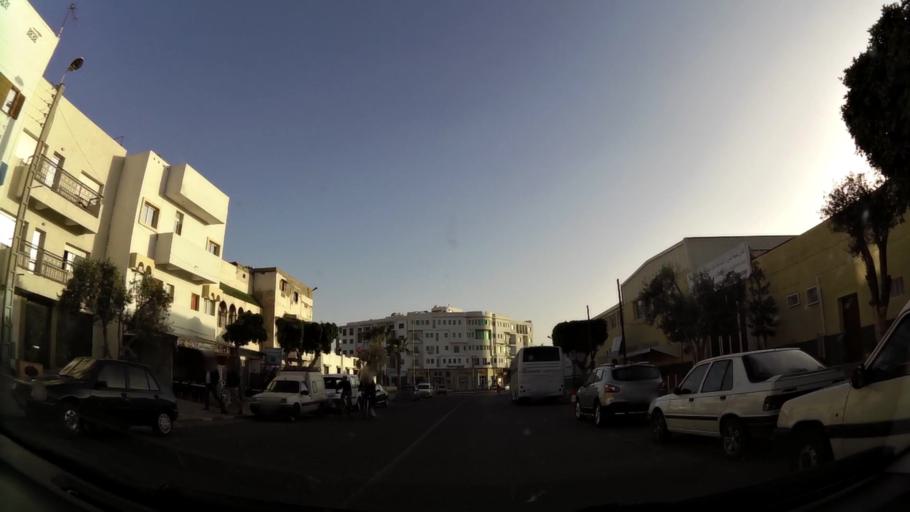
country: MA
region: Oued ed Dahab-Lagouira
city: Dakhla
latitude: 30.4175
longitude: -9.5734
